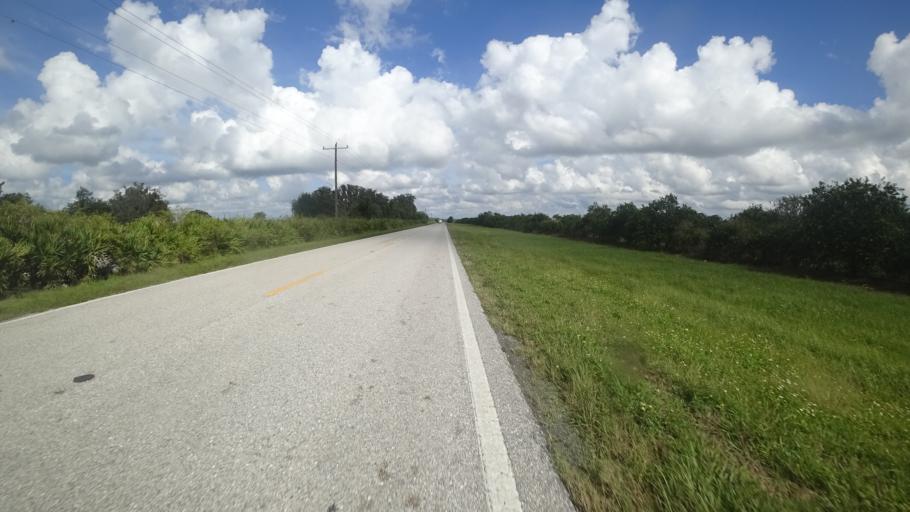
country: US
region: Florida
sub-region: Hillsborough County
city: Wimauma
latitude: 27.5763
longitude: -82.1044
